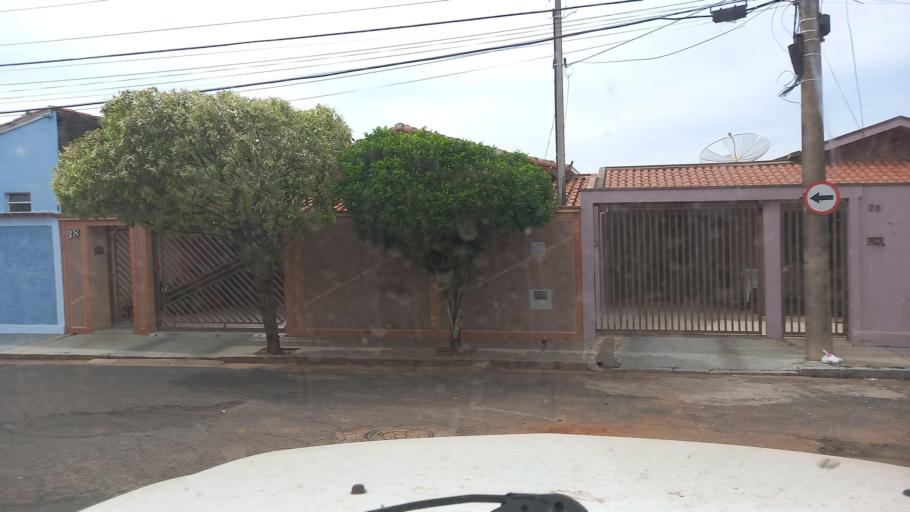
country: BR
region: Sao Paulo
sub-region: Moji-Guacu
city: Mogi-Gaucu
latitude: -22.3592
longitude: -46.9437
